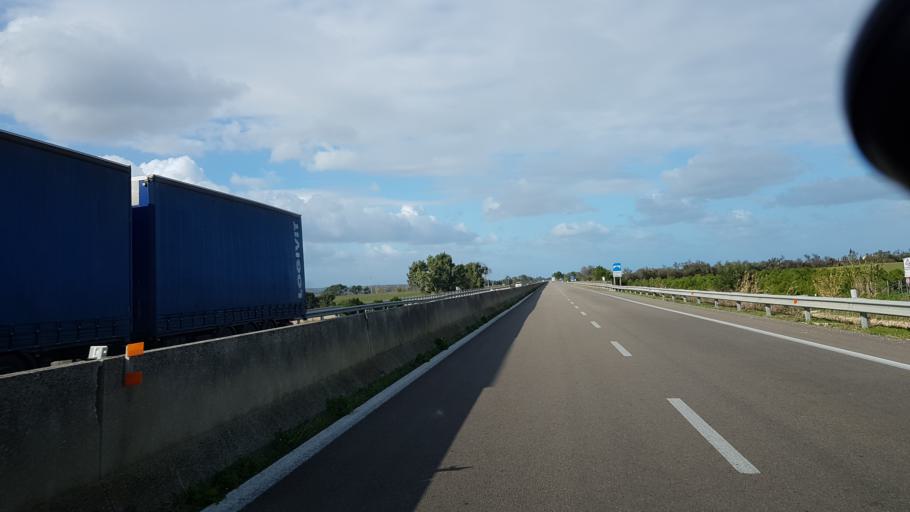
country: IT
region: Apulia
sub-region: Provincia di Brindisi
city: San Vito dei Normanni
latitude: 40.6944
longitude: 17.8159
